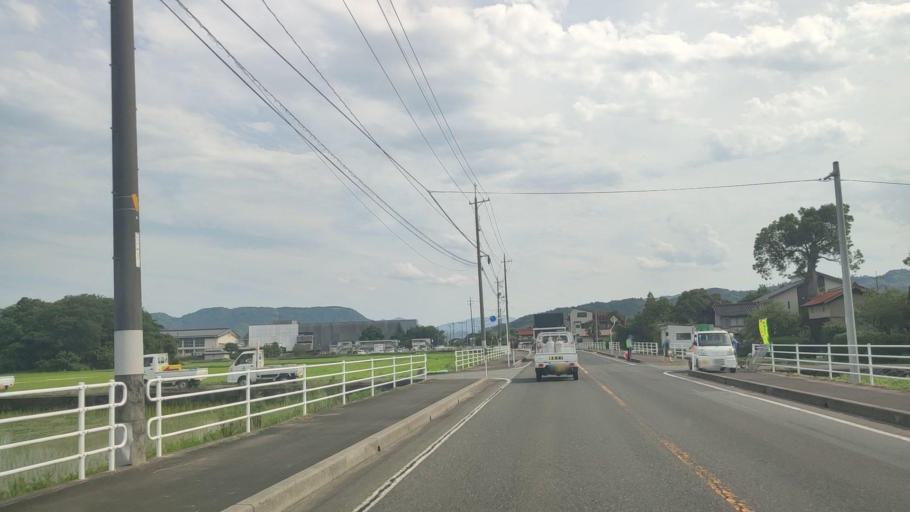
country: JP
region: Tottori
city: Tottori
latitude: 35.4571
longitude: 134.2033
